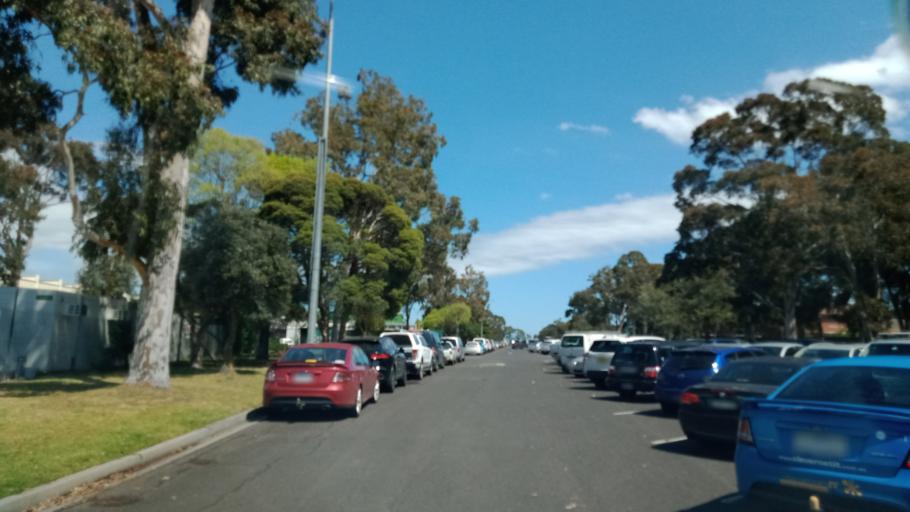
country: AU
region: Victoria
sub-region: Greater Dandenong
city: Springvale
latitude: -37.9503
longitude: 145.1625
